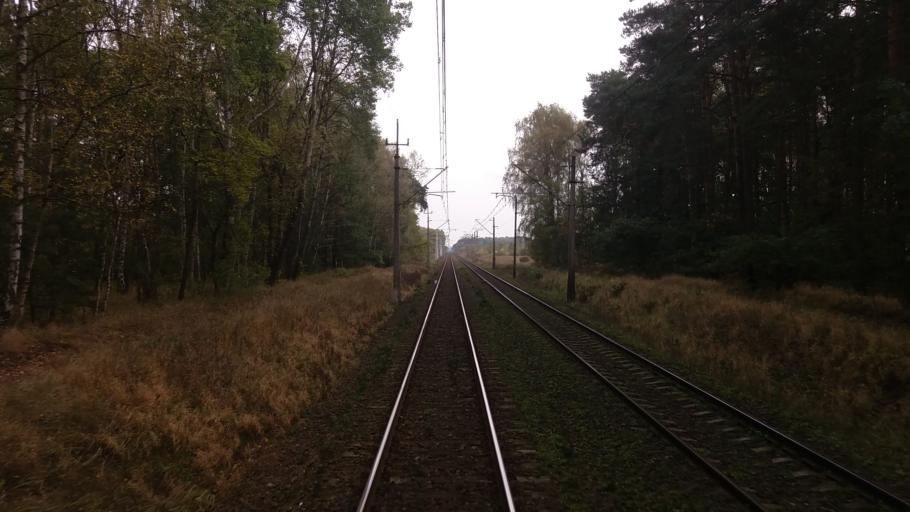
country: PL
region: West Pomeranian Voivodeship
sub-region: Powiat stargardzki
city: Kobylanka
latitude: 53.3681
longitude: 14.8991
